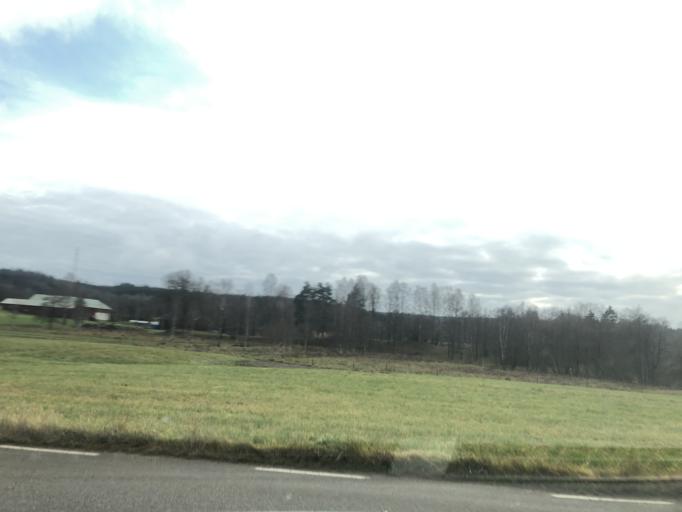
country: SE
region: Vaestra Goetaland
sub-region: Boras Kommun
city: Dalsjofors
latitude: 57.8296
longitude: 13.1714
